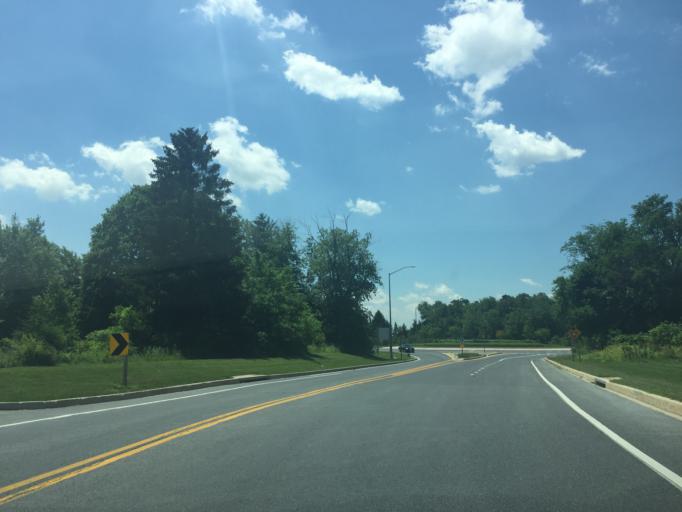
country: US
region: Maryland
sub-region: Carroll County
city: Hampstead
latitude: 39.5829
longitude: -76.8418
